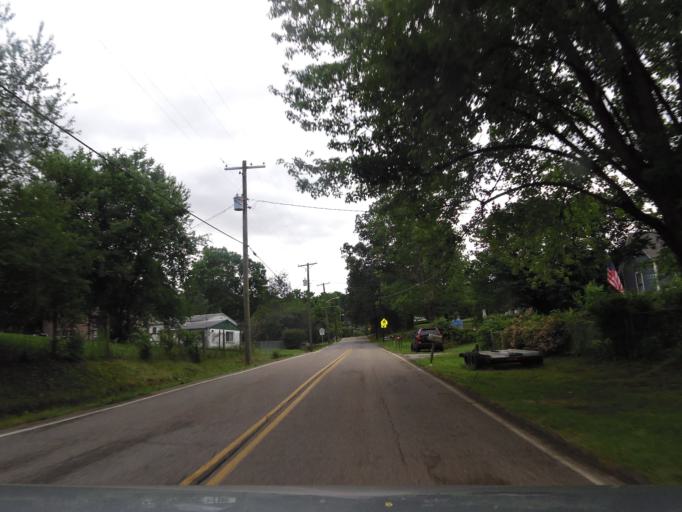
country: US
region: Tennessee
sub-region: Knox County
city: Knoxville
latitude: 35.9657
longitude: -83.9594
